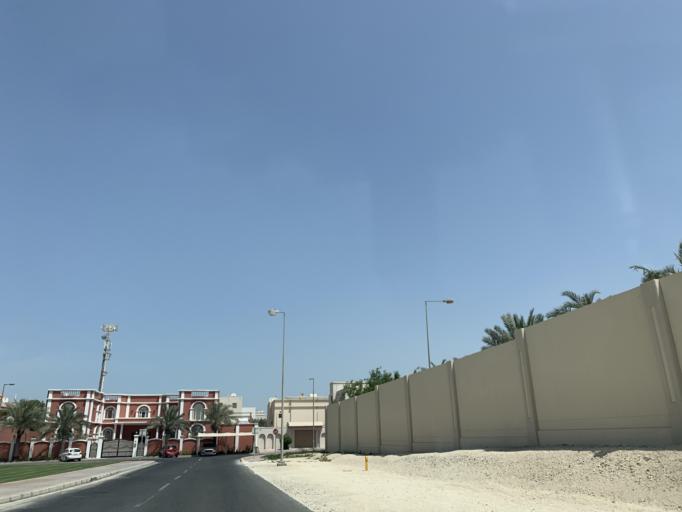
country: BH
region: Northern
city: Ar Rifa'
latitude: 26.1427
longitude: 50.5538
